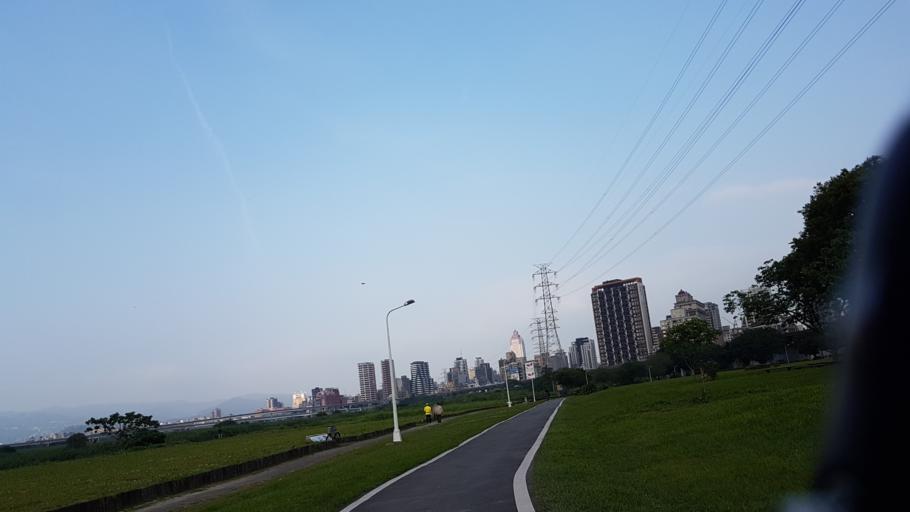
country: TW
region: Taipei
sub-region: Taipei
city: Banqiao
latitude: 25.0380
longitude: 121.4913
